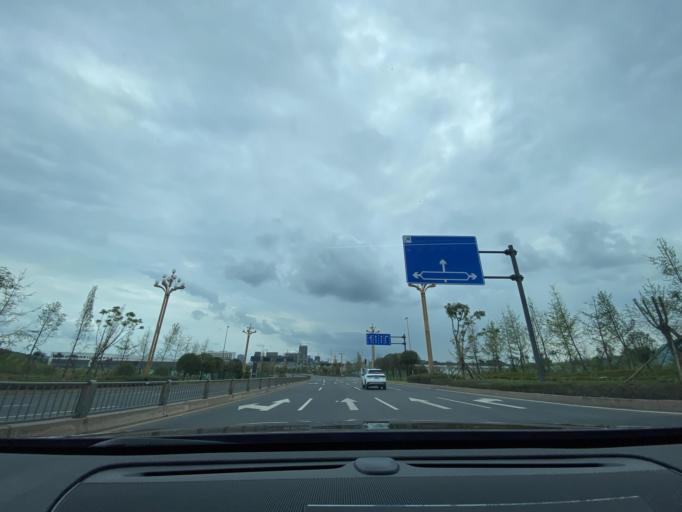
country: CN
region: Sichuan
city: Jiancheng
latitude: 30.4448
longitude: 104.4961
